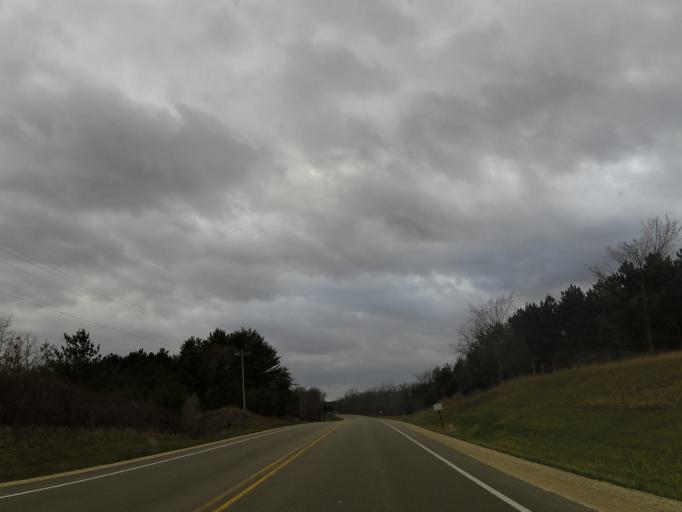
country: US
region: Wisconsin
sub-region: Saint Croix County
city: Roberts
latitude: 45.0478
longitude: -92.6189
